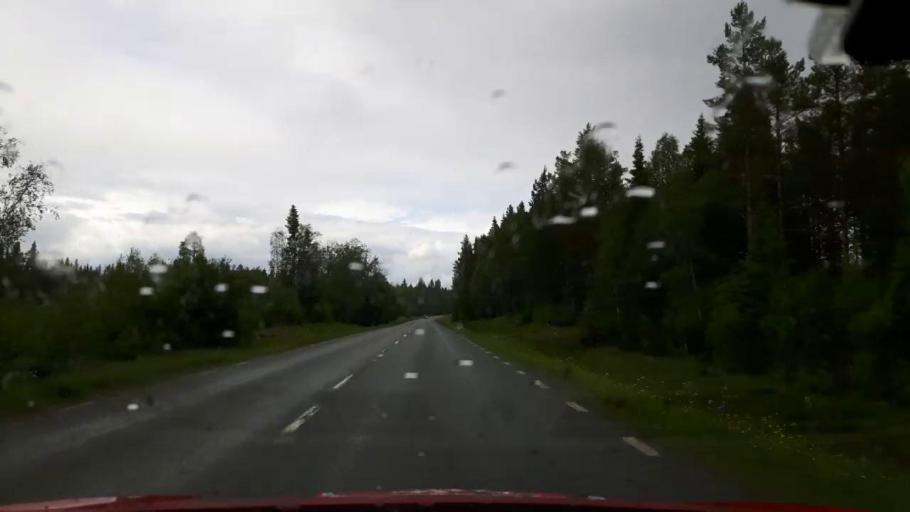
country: SE
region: Jaemtland
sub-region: Krokoms Kommun
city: Krokom
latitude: 63.4436
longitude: 14.1973
